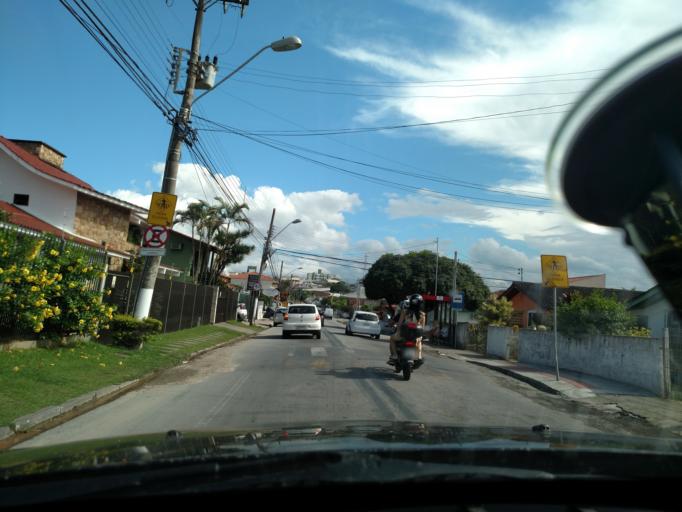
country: BR
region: Santa Catarina
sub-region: Sao Jose
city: Campinas
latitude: -27.6021
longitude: -48.6396
